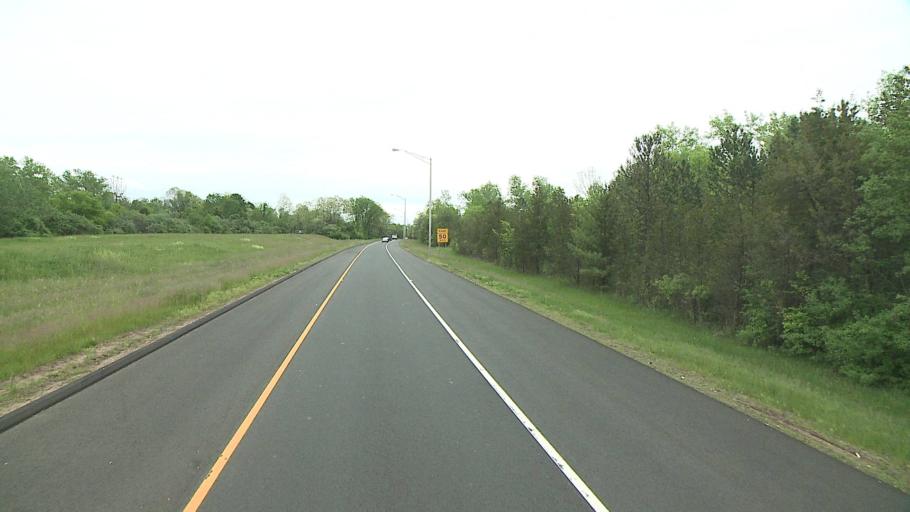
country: US
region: Connecticut
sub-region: Hartford County
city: West Hartford
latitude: 41.7254
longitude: -72.7778
